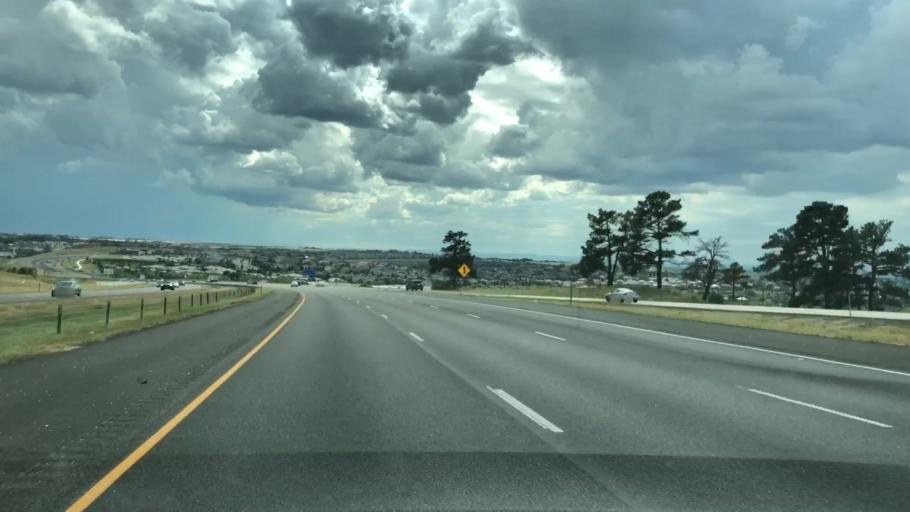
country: US
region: Colorado
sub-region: Douglas County
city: Parker
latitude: 39.5941
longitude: -104.7106
